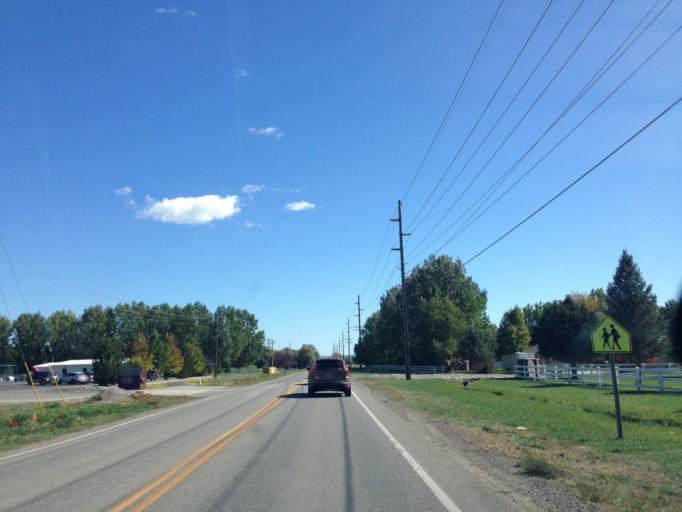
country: US
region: Montana
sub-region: Yellowstone County
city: Billings
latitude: 45.7840
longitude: -108.6320
